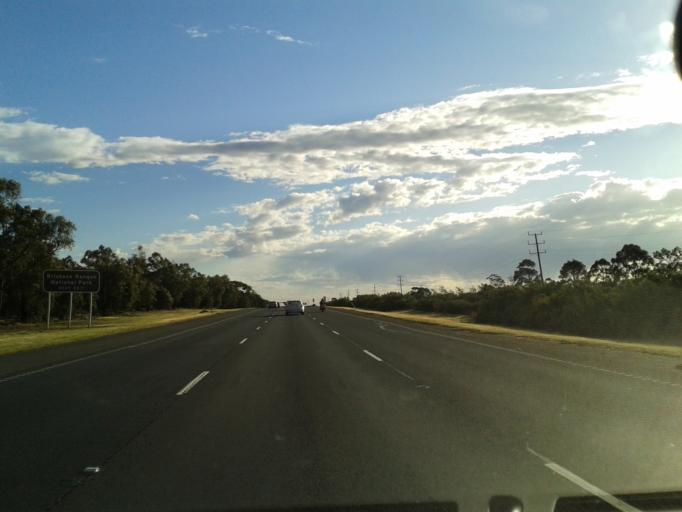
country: AU
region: Victoria
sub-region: Wyndham
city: Little River
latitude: -37.9617
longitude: 144.5702
